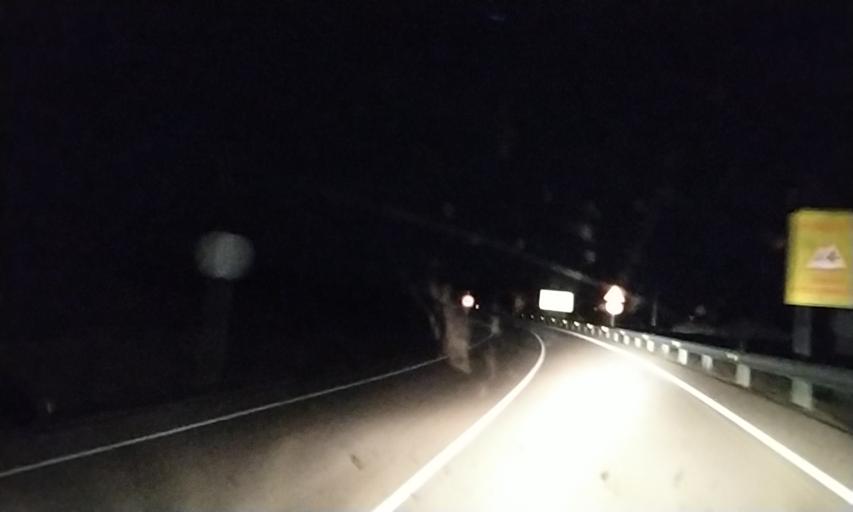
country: ES
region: Castille and Leon
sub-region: Provincia de Salamanca
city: Herguijuela de Ciudad Rodrigo
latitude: 40.4785
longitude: -6.5776
